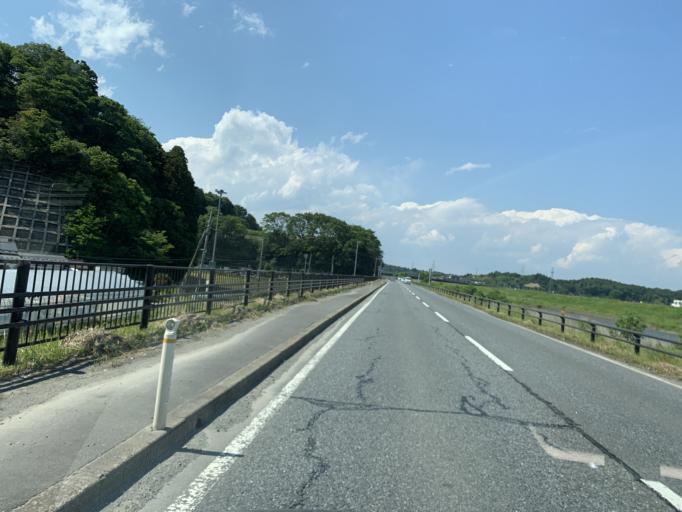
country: JP
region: Miyagi
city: Yamoto
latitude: 38.4080
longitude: 141.1460
